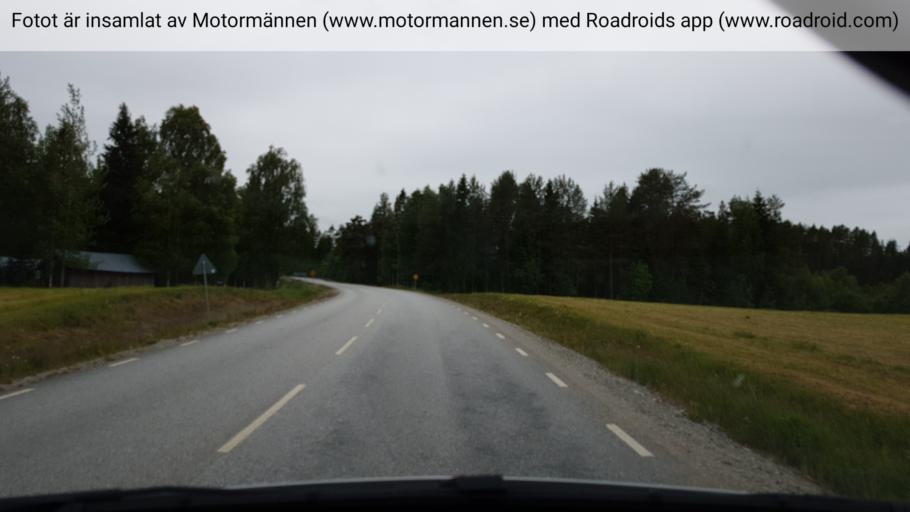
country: SE
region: Vaesterbotten
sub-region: Vindelns Kommun
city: Vindeln
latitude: 64.2004
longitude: 19.4150
